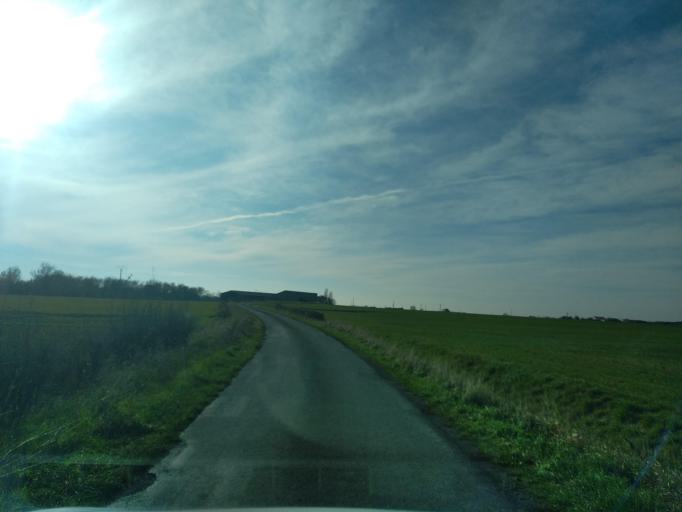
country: FR
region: Pays de la Loire
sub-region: Departement de la Vendee
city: Maillezais
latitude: 46.3534
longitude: -0.7441
